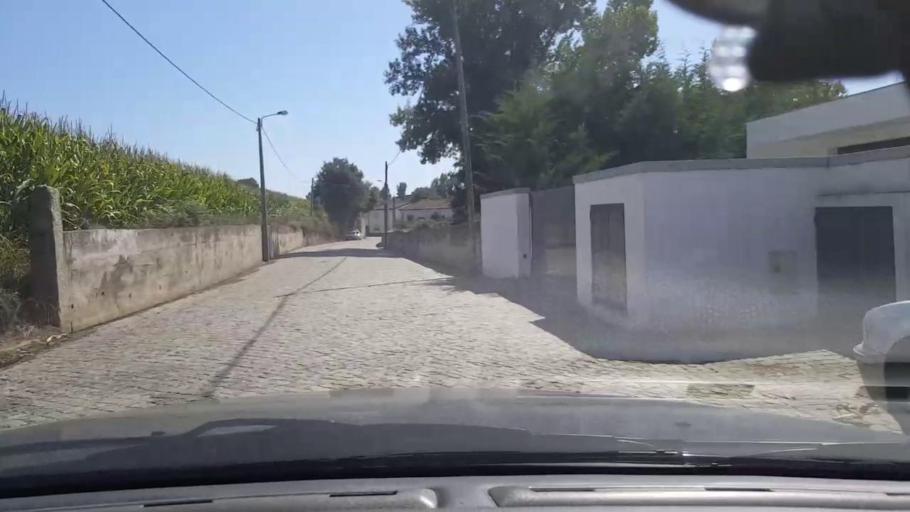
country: PT
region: Porto
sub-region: Matosinhos
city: Lavra
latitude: 41.2722
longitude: -8.6930
